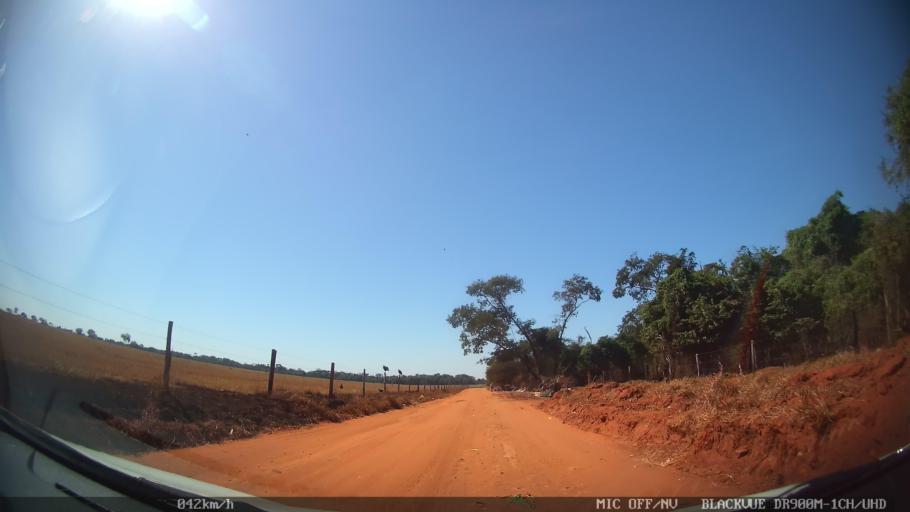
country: BR
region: Sao Paulo
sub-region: Sao Jose Do Rio Preto
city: Sao Jose do Rio Preto
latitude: -20.7423
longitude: -49.4294
